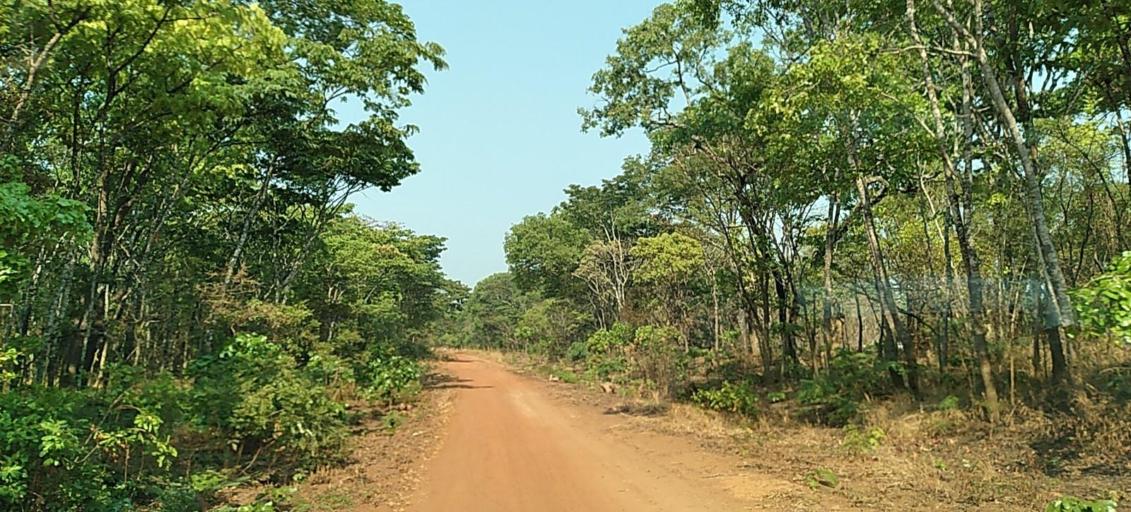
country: ZM
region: Copperbelt
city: Chingola
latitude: -12.8806
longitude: 27.4339
